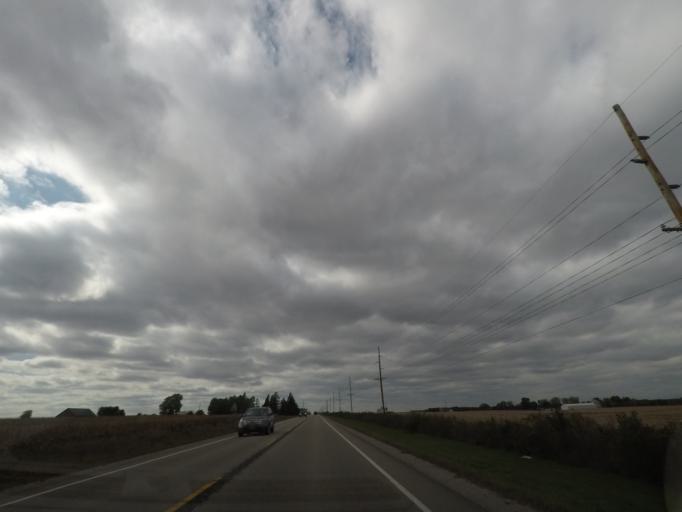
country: US
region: Iowa
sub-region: Story County
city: Huxley
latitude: 41.8778
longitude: -93.5516
